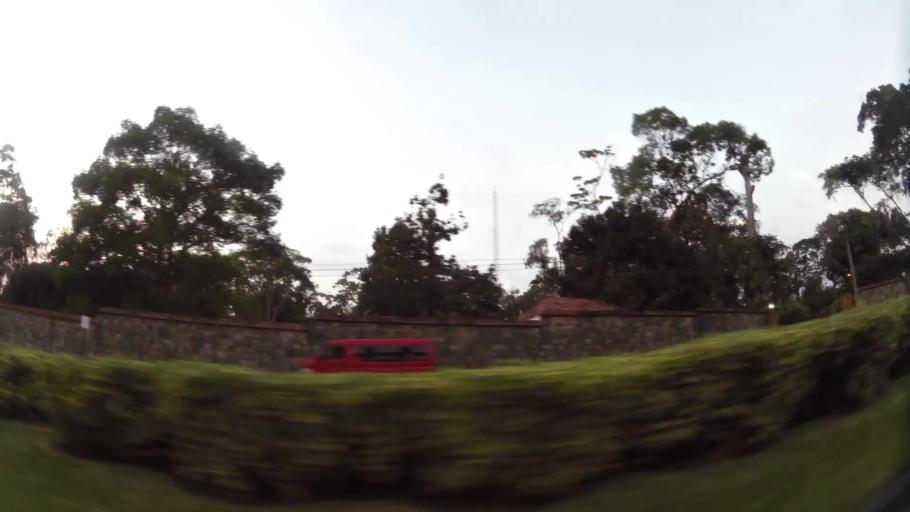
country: GT
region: Retalhuleu
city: Santa Cruz Mulua
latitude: 14.5963
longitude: -91.6153
